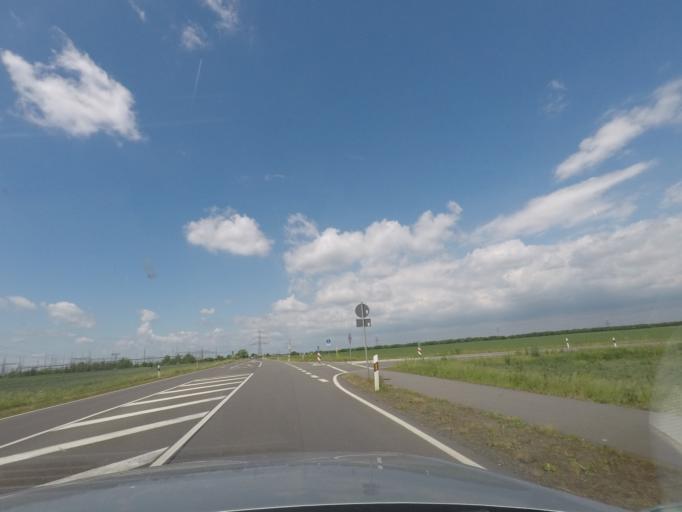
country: DE
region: Saxony
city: Zwenkau
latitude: 51.1955
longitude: 12.3442
